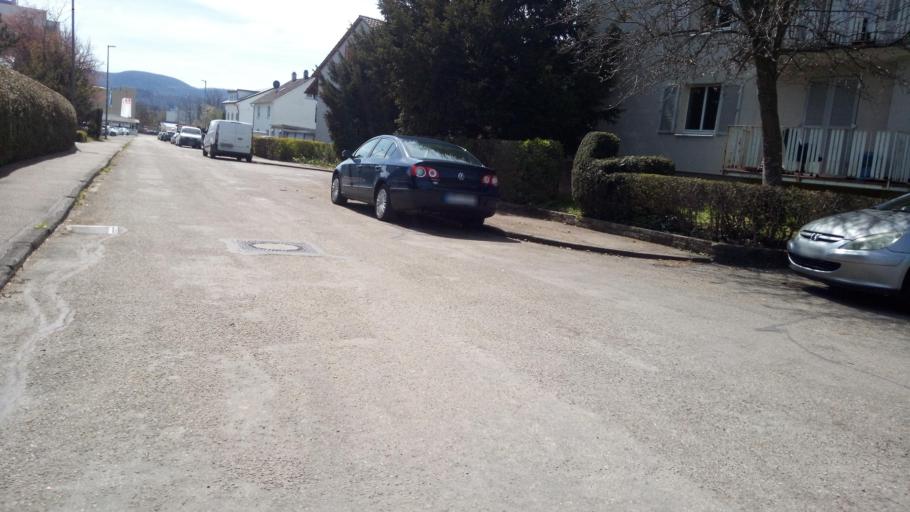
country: DE
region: Baden-Wuerttemberg
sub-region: Regierungsbezirk Stuttgart
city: Sussen
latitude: 48.6866
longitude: 9.7728
